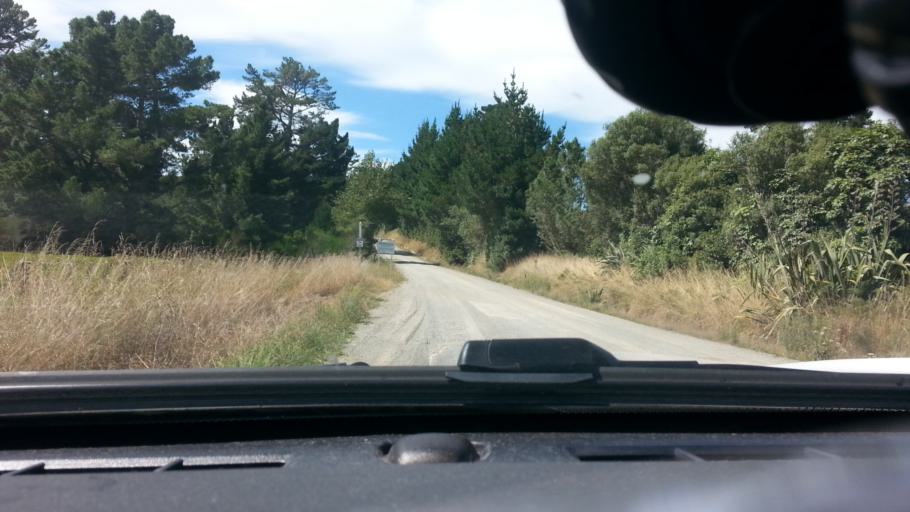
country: NZ
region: Wellington
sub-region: Masterton District
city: Masterton
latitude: -41.0588
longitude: 175.9331
